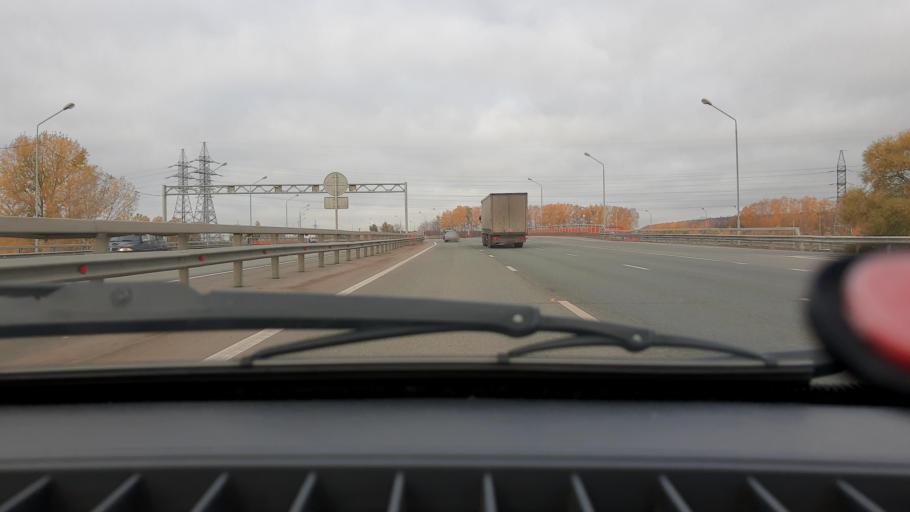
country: RU
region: Bashkortostan
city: Avdon
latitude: 54.6769
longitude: 55.8058
